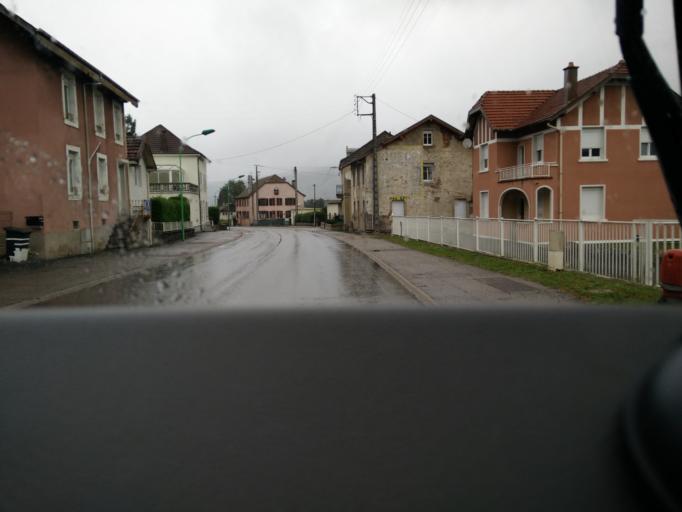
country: FR
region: Lorraine
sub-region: Departement des Vosges
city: Plainfaing
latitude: 48.1793
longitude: 7.0077
